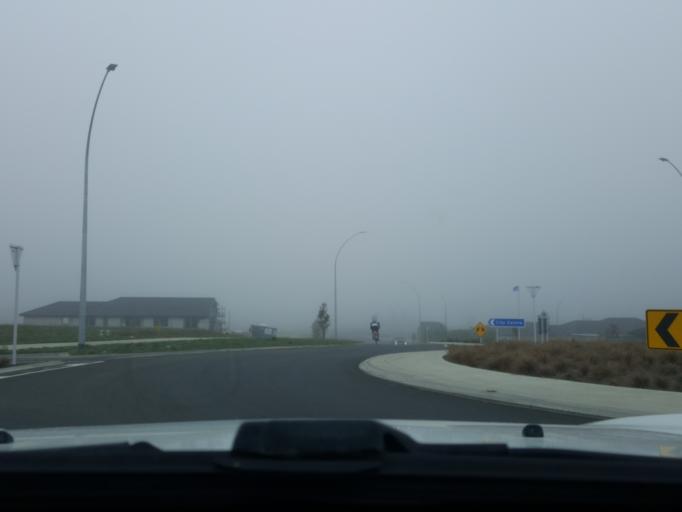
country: NZ
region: Waikato
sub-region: Hamilton City
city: Hamilton
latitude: -37.7639
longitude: 175.2239
